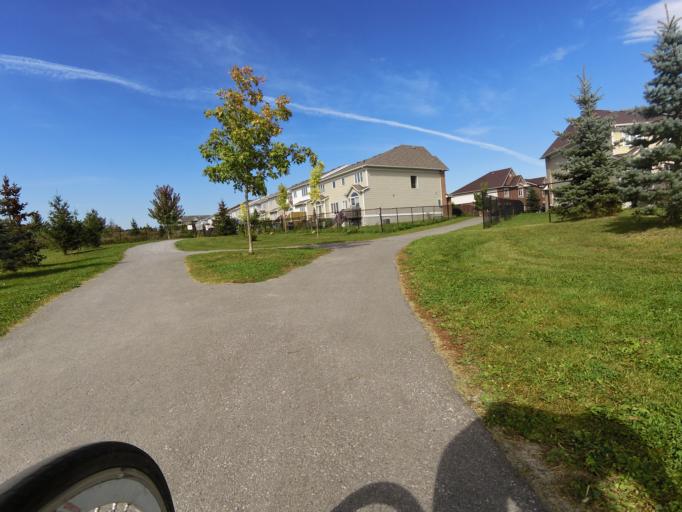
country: CA
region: Ontario
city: Bells Corners
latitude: 45.2681
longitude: -75.7291
